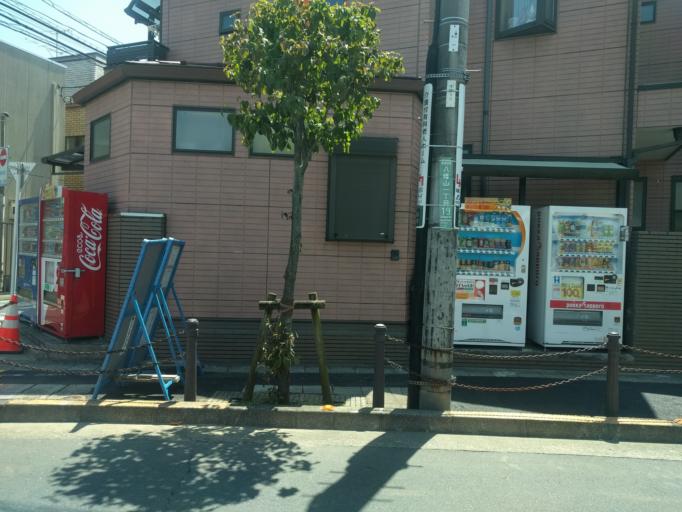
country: JP
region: Tokyo
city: Mitaka-shi
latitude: 35.6629
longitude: 139.6223
